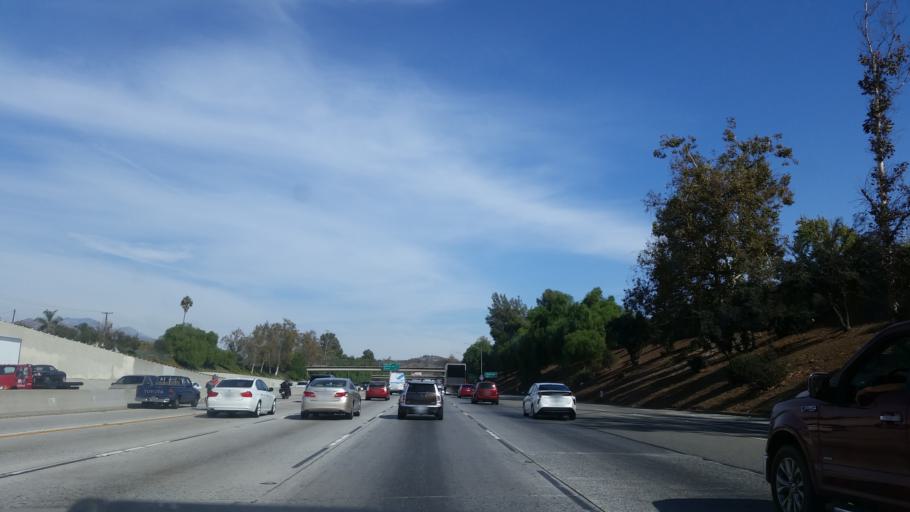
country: US
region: California
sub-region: Los Angeles County
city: Citrus
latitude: 34.1207
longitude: -117.8880
